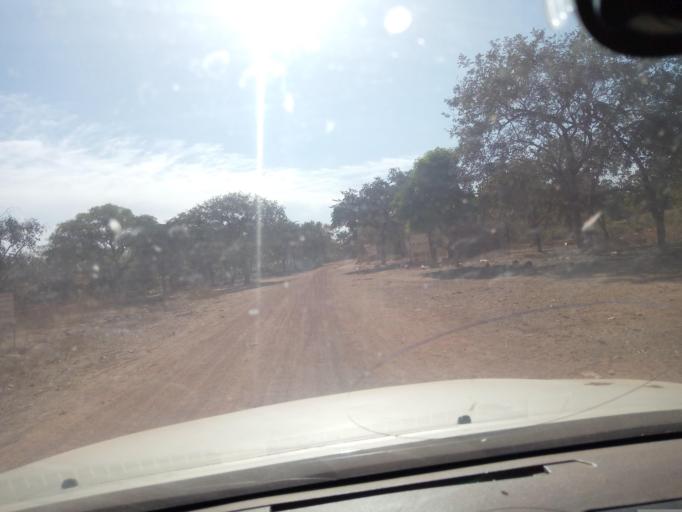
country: ML
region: Sikasso
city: Sikasso
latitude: 11.4607
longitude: -5.3253
